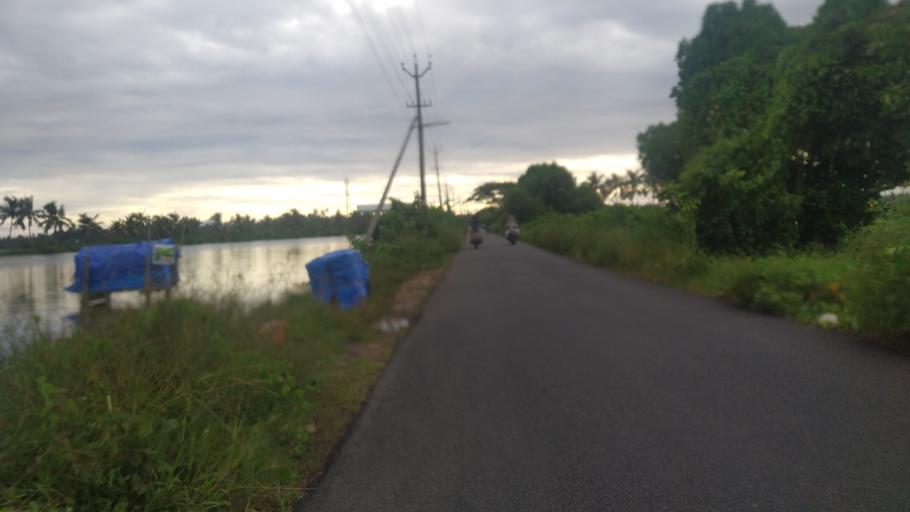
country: IN
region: Kerala
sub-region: Alappuzha
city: Arukutti
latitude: 9.8577
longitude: 76.2753
